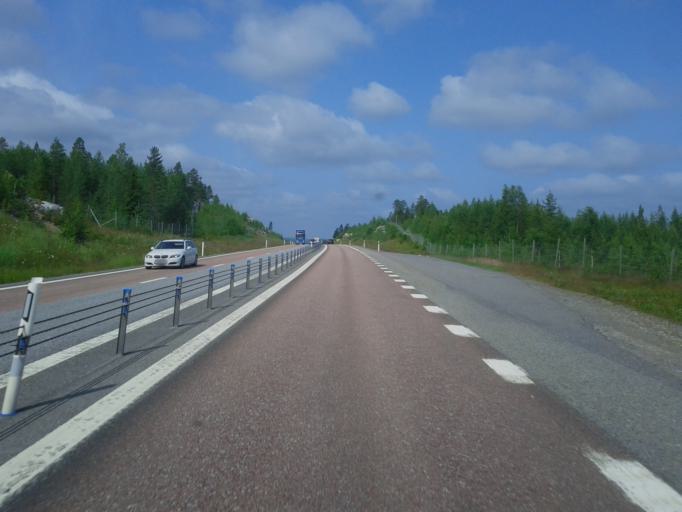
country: SE
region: Vaesterbotten
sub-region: Skelleftea Kommun
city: Soedra Bergsbyn
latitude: 64.6860
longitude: 21.0580
